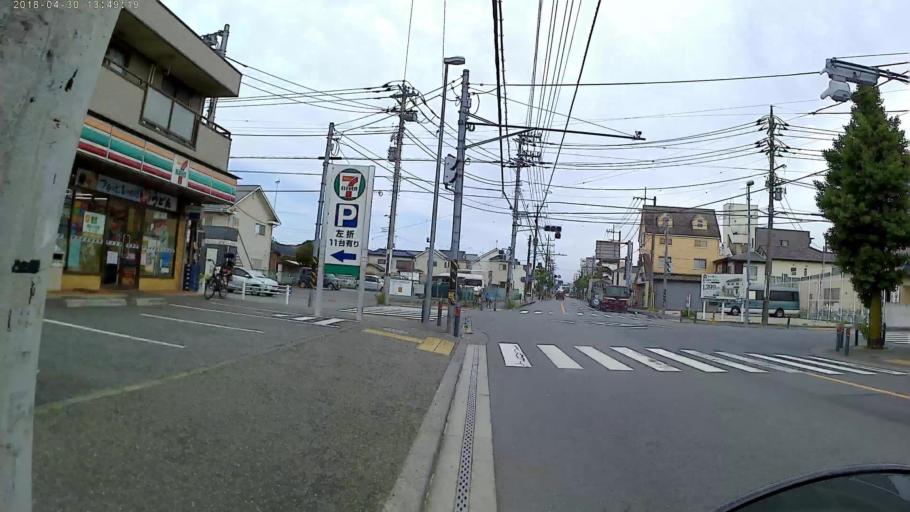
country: JP
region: Tokyo
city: Hachioji
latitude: 35.5920
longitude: 139.3682
